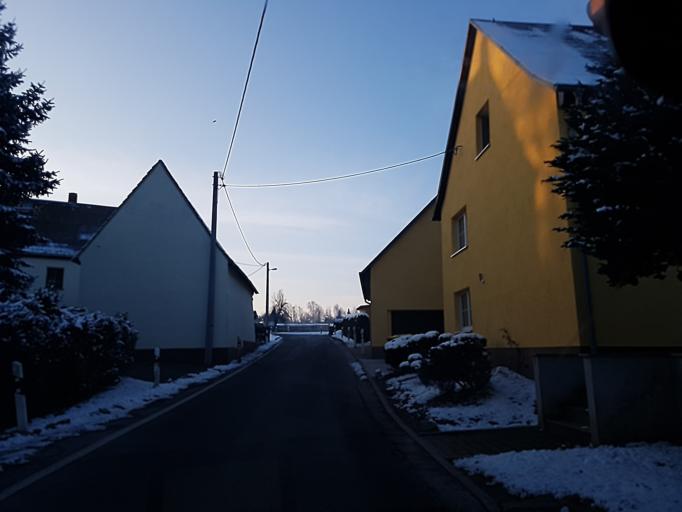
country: DE
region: Saxony
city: Grossweitzschen
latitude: 51.1786
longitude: 13.0405
